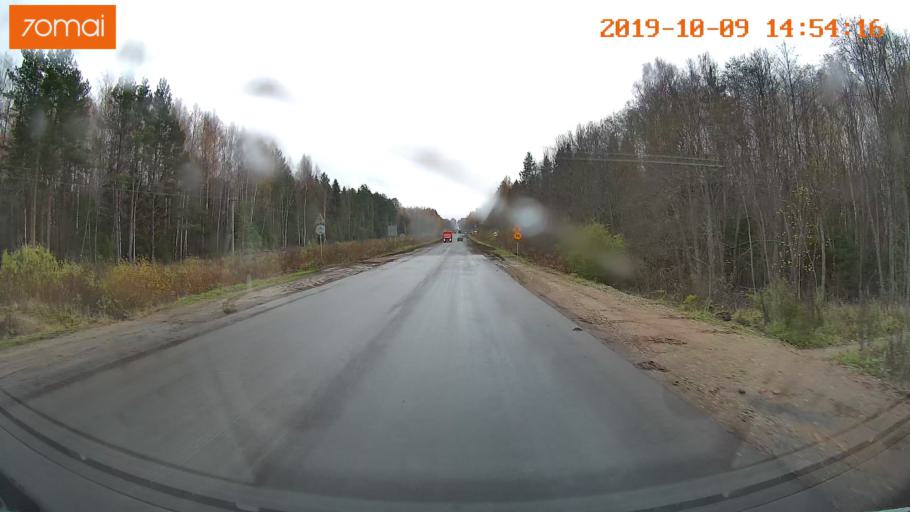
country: RU
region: Kostroma
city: Chistyye Bory
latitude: 58.3583
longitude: 41.6422
